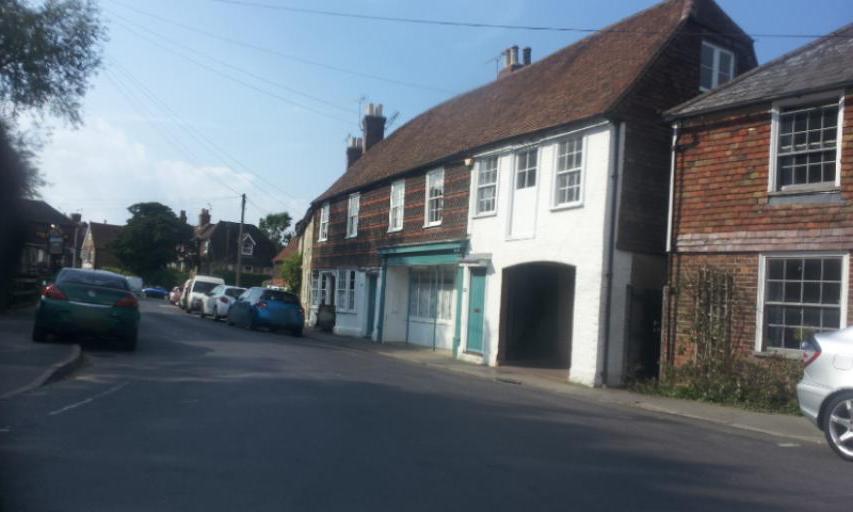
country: GB
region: England
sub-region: Kent
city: Harrietsham
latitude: 51.2422
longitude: 0.6750
